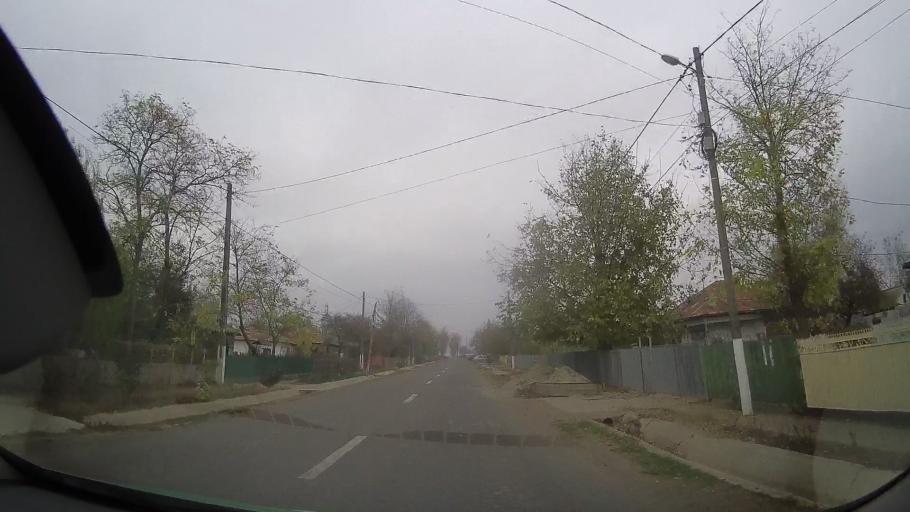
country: RO
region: Braila
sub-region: Comuna Rosiori
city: Rosiori
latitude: 44.8129
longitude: 27.3896
